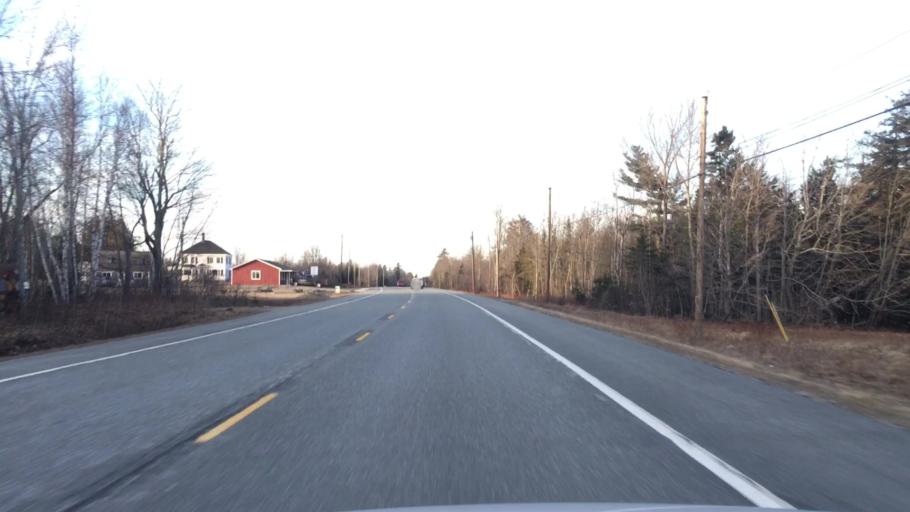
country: US
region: Maine
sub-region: Hancock County
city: Surry
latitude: 44.6000
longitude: -68.5140
